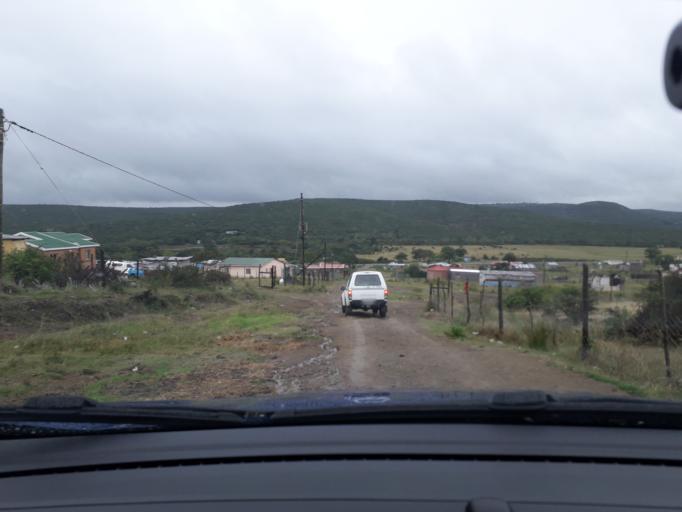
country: ZA
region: Eastern Cape
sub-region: Buffalo City Metropolitan Municipality
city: Bhisho
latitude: -32.8073
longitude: 27.3663
